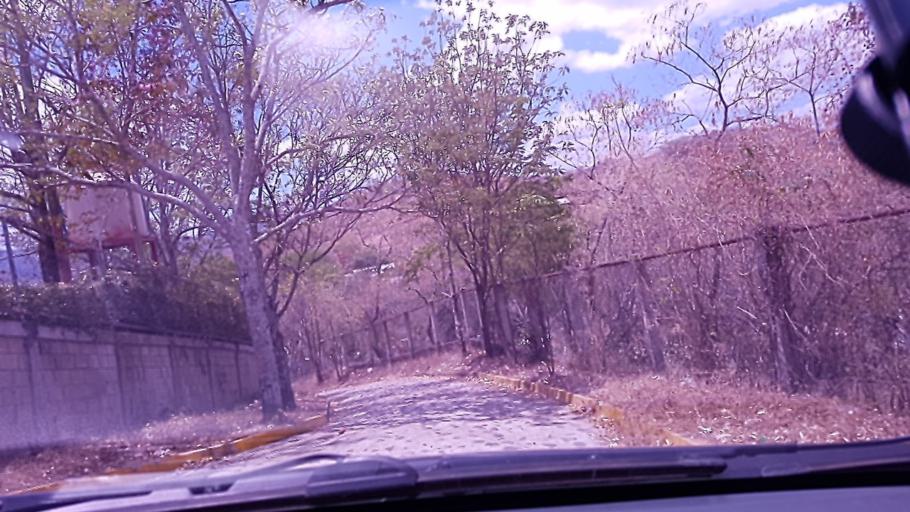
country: NI
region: Esteli
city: Condega
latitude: 13.3600
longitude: -86.3997
